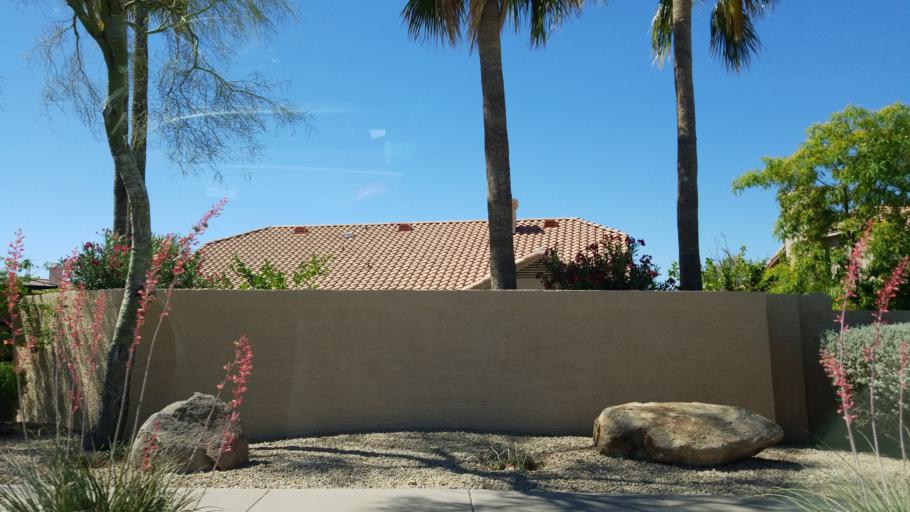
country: US
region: Arizona
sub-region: Maricopa County
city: Fountain Hills
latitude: 33.5896
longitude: -111.8015
